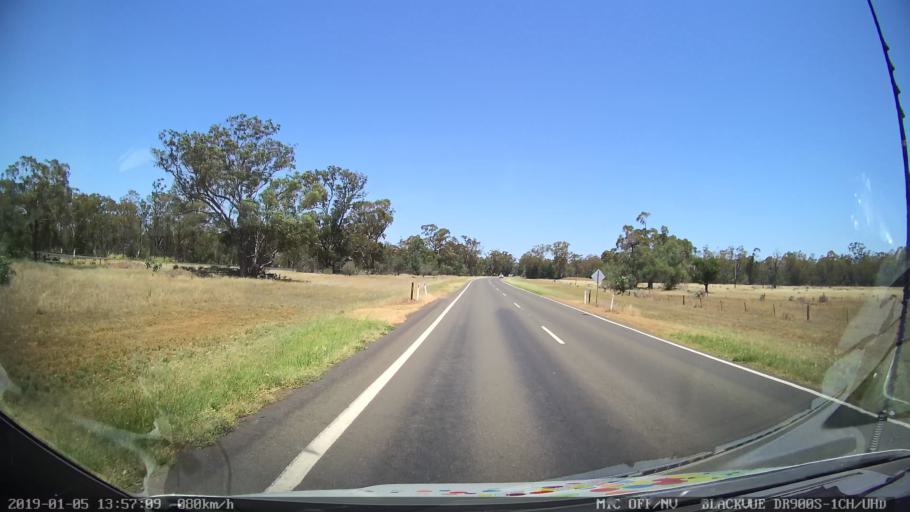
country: AU
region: New South Wales
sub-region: Gunnedah
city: Gunnedah
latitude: -31.1244
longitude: 150.2727
